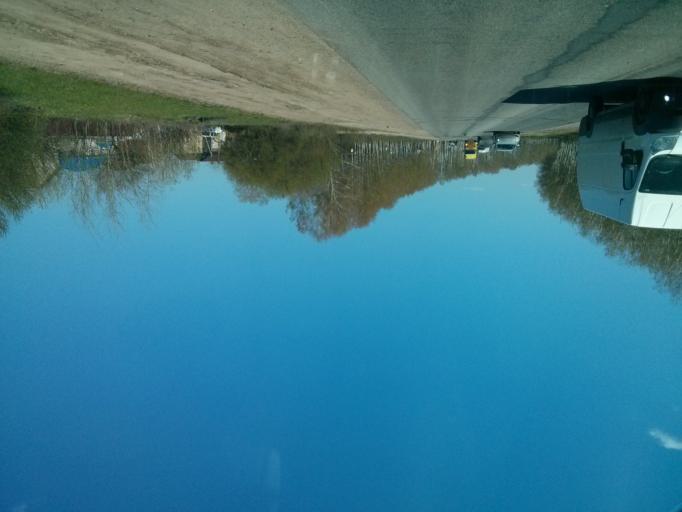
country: RU
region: Nizjnij Novgorod
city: Nizhniy Novgorod
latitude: 56.2137
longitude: 43.9661
